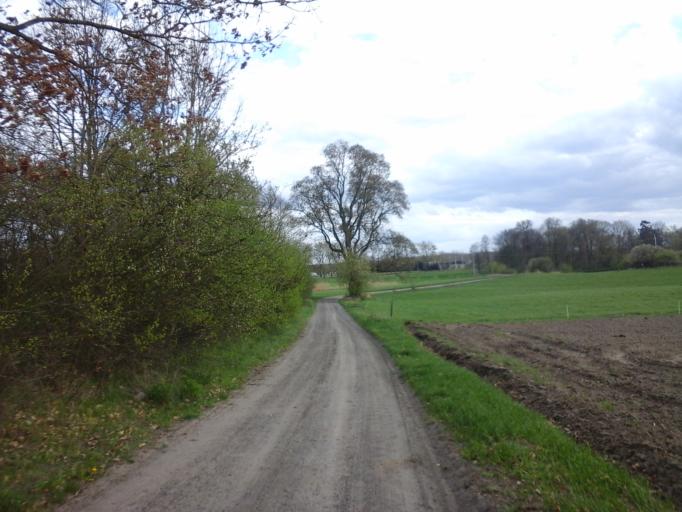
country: PL
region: West Pomeranian Voivodeship
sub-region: Powiat choszczenski
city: Bierzwnik
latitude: 53.0611
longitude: 15.5934
